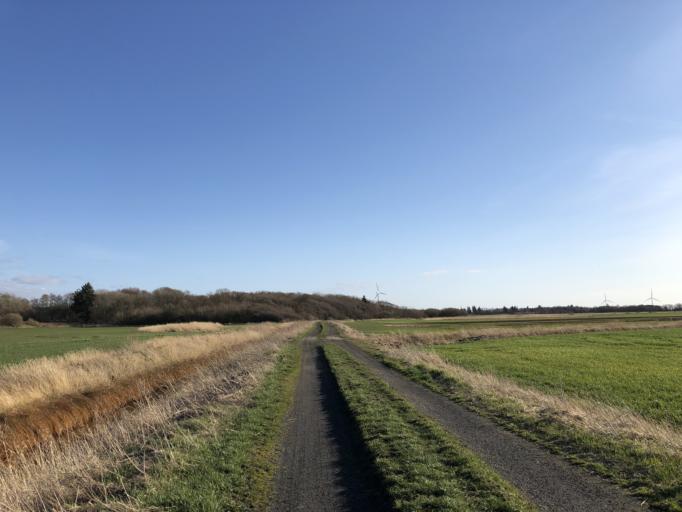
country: DK
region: Central Jutland
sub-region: Holstebro Kommune
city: Ulfborg
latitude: 56.3302
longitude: 8.3269
